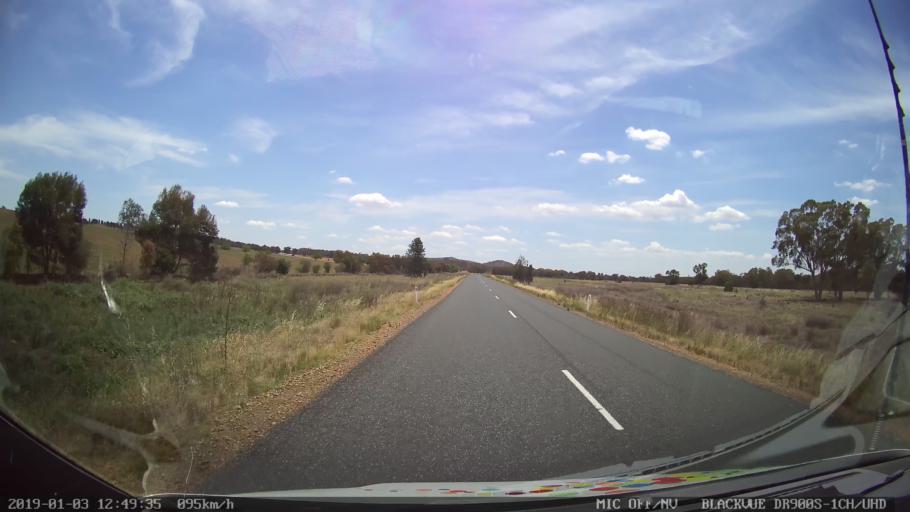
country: AU
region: New South Wales
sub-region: Weddin
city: Grenfell
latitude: -33.7017
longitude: 148.2623
